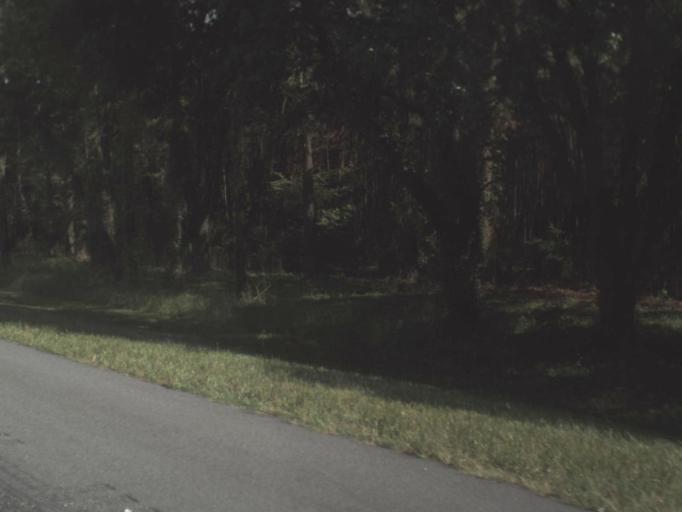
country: US
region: Florida
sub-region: Suwannee County
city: Wellborn
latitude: 30.2695
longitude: -82.7677
